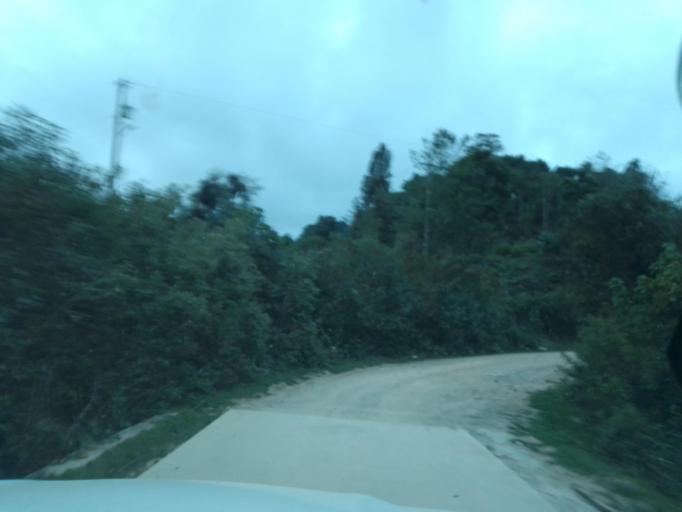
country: MX
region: Chiapas
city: Motozintla de Mendoza
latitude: 15.2257
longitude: -92.2392
